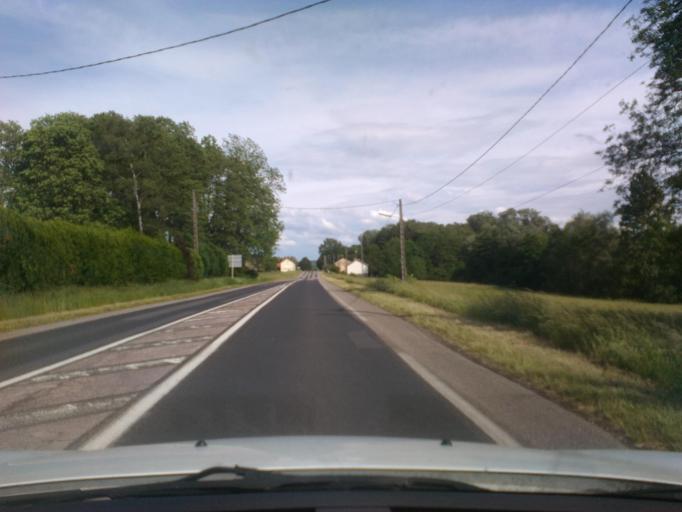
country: FR
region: Lorraine
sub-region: Departement de Meurthe-et-Moselle
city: Baccarat
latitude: 48.4824
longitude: 6.7028
